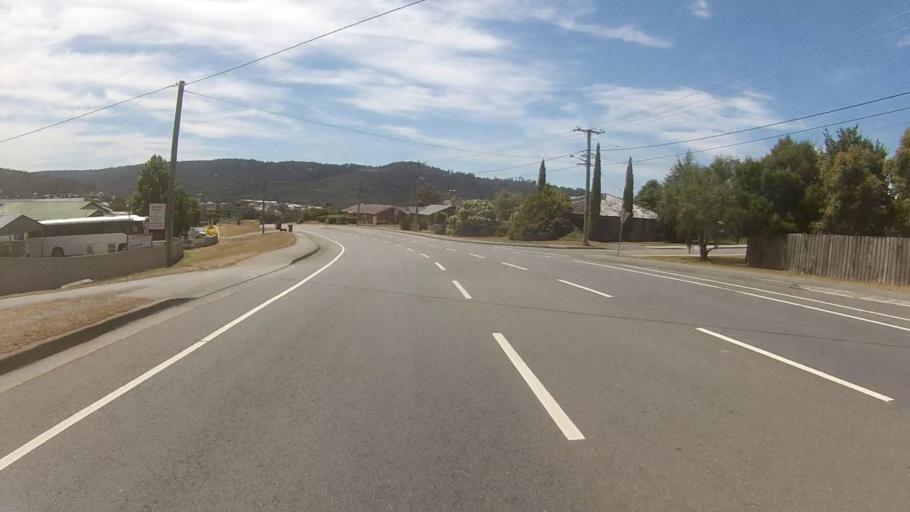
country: AU
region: Tasmania
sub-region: Kingborough
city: Kingston
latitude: -42.9777
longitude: 147.3025
